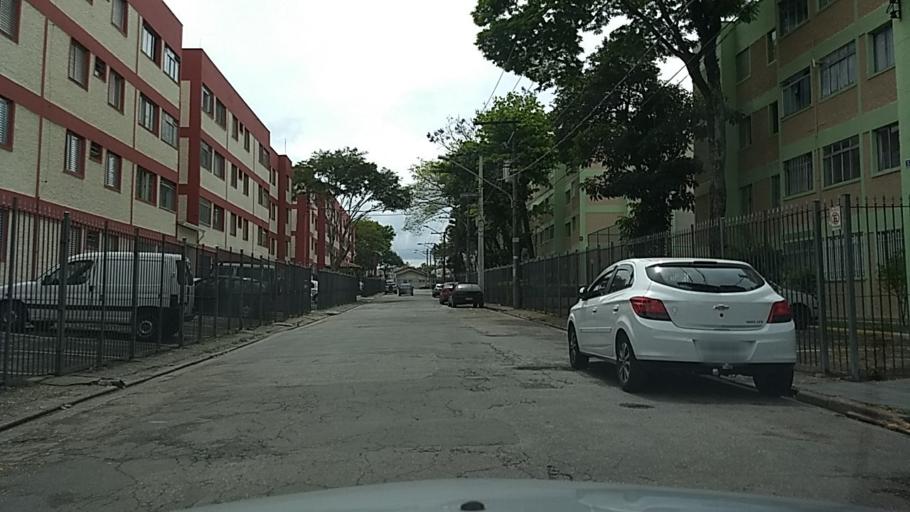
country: BR
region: Sao Paulo
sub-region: Guarulhos
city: Guarulhos
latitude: -23.4724
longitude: -46.5821
